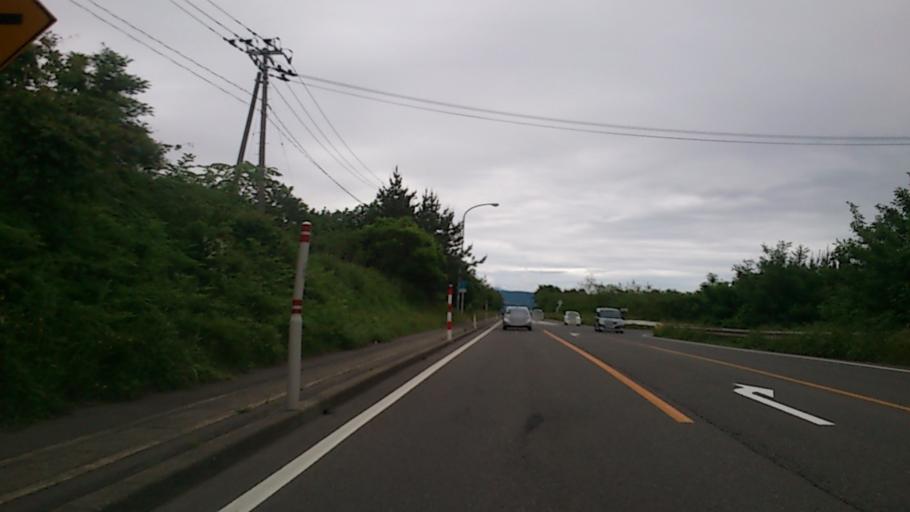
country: JP
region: Akita
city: Akita Shi
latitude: 39.3754
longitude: 140.0177
